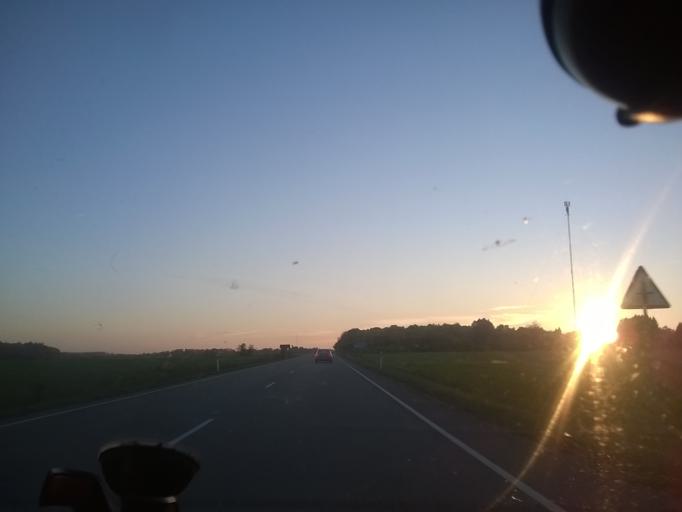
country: EE
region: Laeaene
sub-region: Ridala Parish
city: Uuemoisa
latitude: 58.9705
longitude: 23.8409
